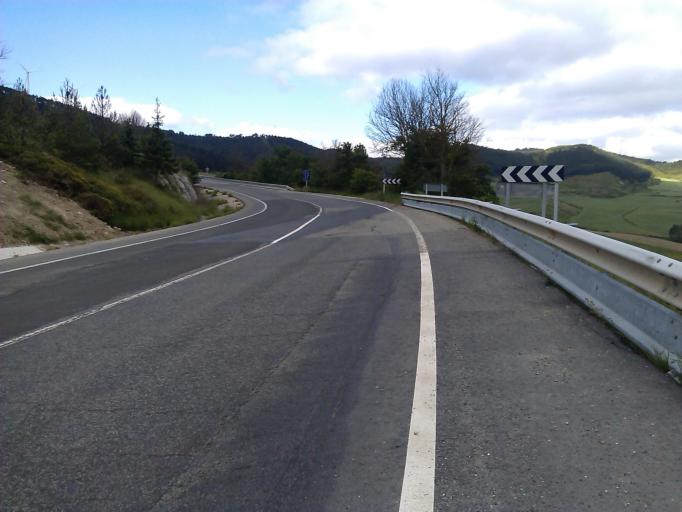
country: ES
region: Navarre
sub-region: Provincia de Navarra
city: Uterga
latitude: 42.7479
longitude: -1.7548
